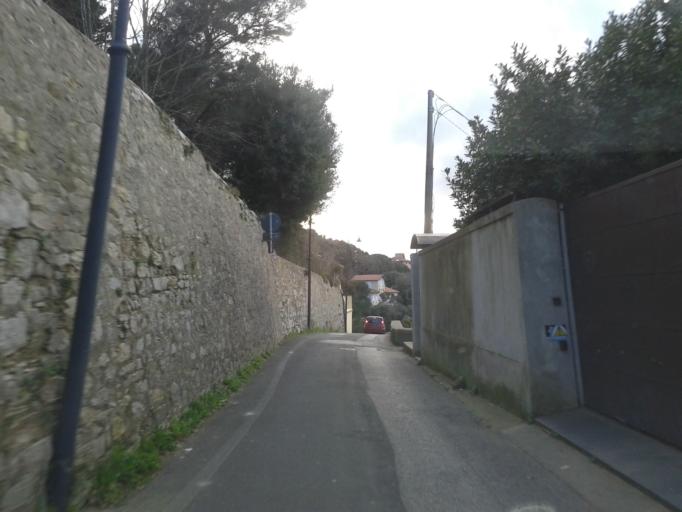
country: IT
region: Tuscany
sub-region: Provincia di Livorno
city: Quercianella
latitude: 43.4941
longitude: 10.3502
